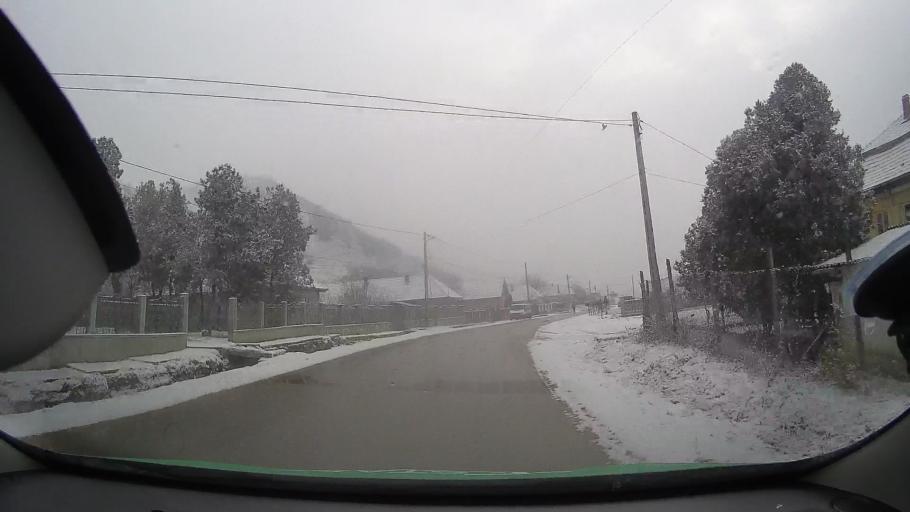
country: RO
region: Alba
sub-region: Comuna Lopadea Noua
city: Lopadea Noua
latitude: 46.2980
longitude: 23.8134
